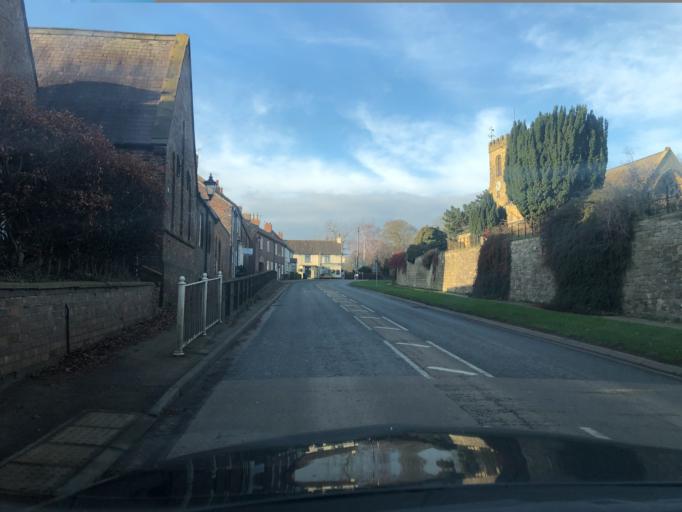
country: GB
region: England
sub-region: North Yorkshire
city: Northallerton
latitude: 54.3231
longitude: -1.4857
